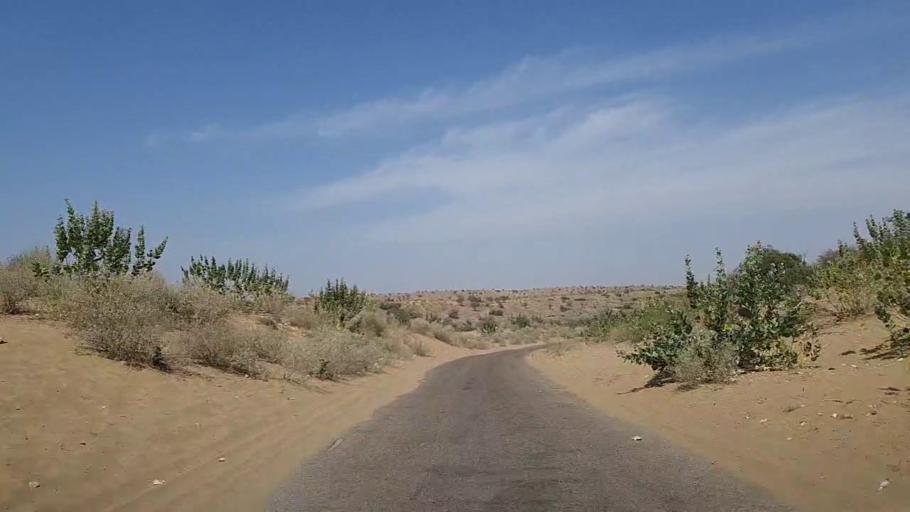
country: PK
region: Sindh
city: Nabisar
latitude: 25.1143
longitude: 69.9974
